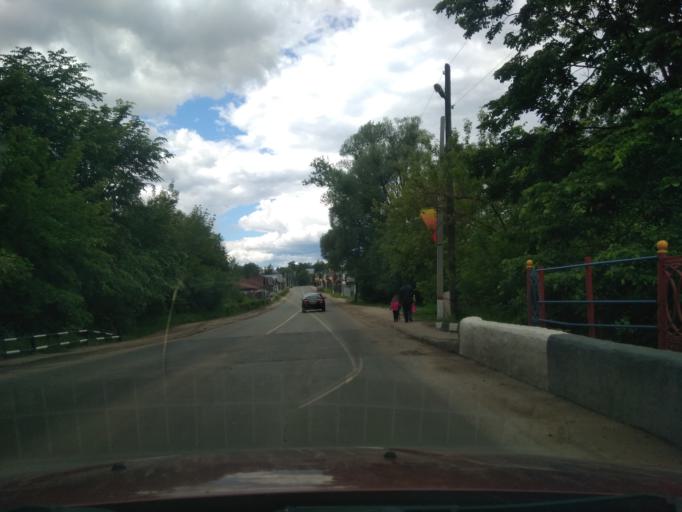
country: RU
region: Vladimir
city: Melenki
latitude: 55.3383
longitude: 41.6246
